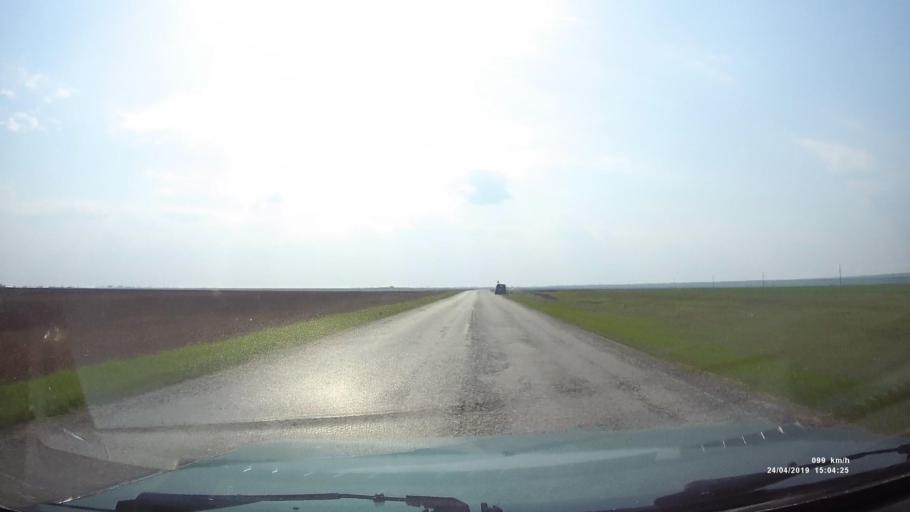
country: RU
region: Rostov
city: Remontnoye
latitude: 46.5622
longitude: 43.4708
